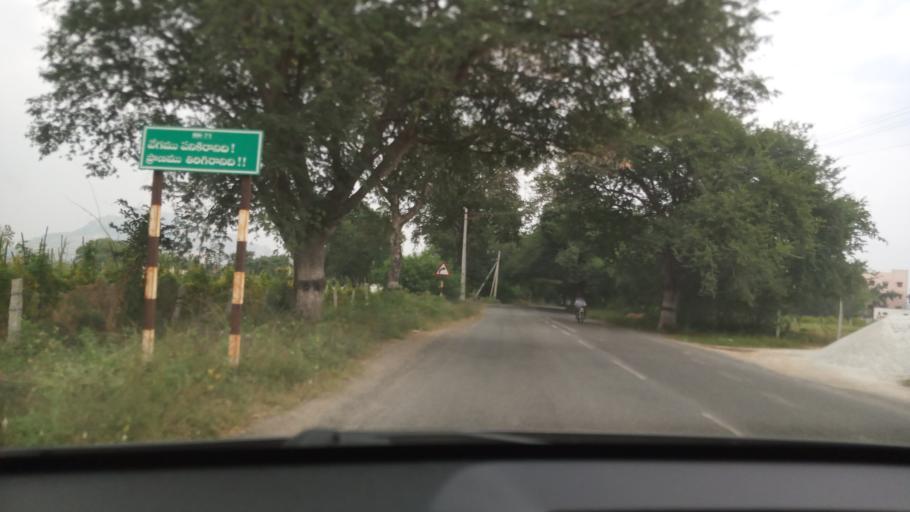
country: IN
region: Andhra Pradesh
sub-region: Chittoor
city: Madanapalle
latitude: 13.6517
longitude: 78.8147
